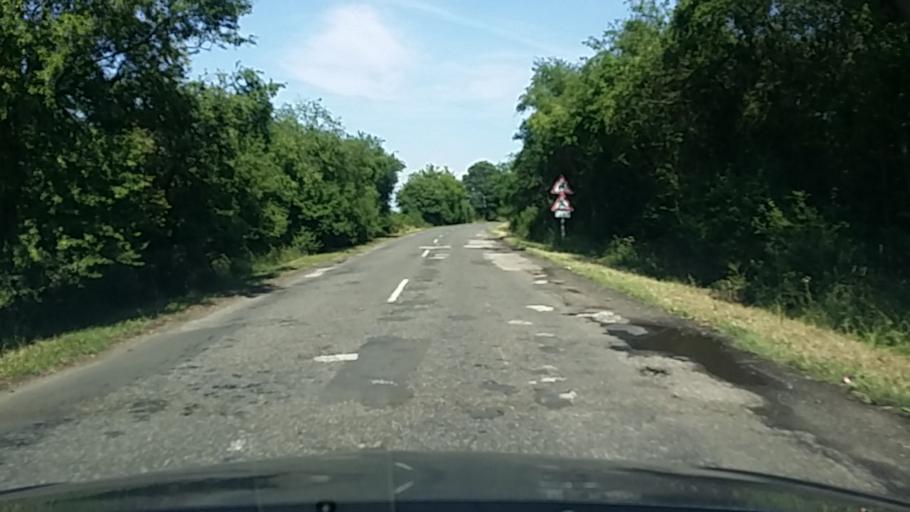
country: SK
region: Nitriansky
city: Sahy
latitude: 48.0587
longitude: 18.9427
